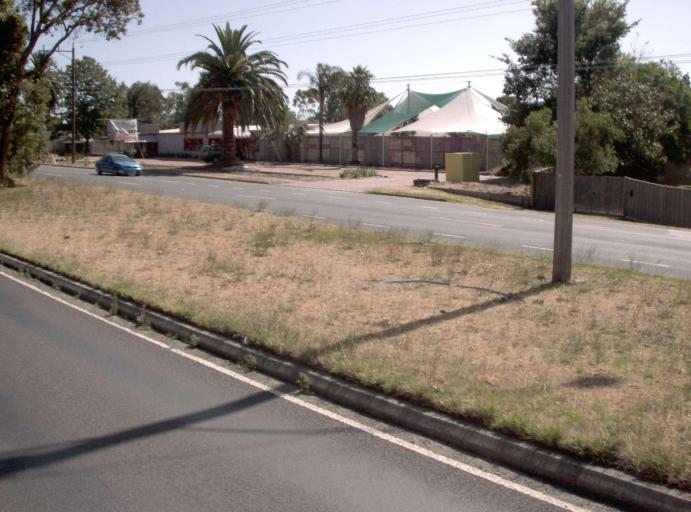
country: AU
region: Victoria
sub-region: Frankston
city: Carrum Downs
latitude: -38.0925
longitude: 145.1785
